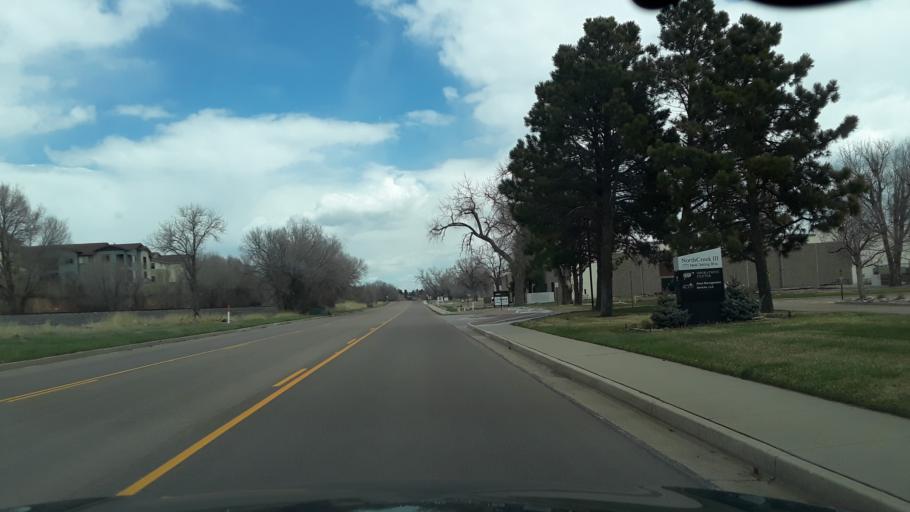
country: US
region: Colorado
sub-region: El Paso County
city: Colorado Springs
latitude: 38.9159
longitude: -104.8215
